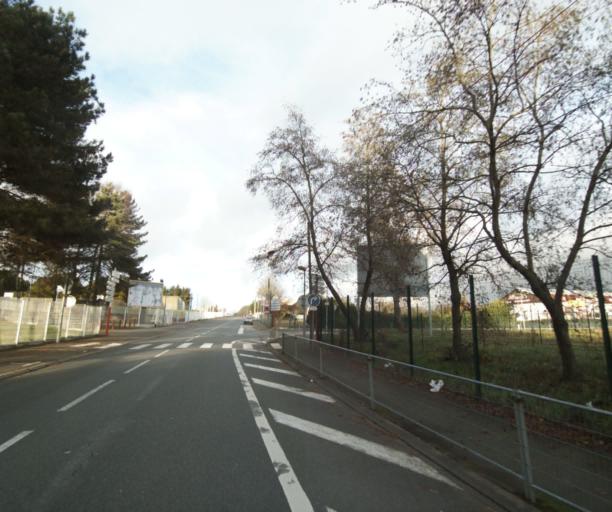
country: FR
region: Pays de la Loire
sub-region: Departement de la Sarthe
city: Arnage
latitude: 47.9600
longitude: 0.2081
